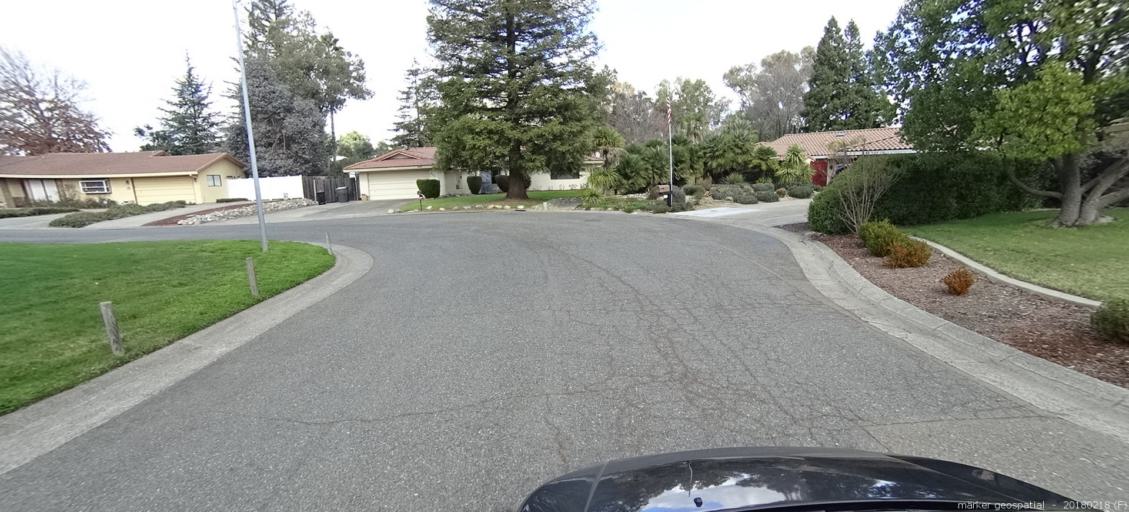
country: US
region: California
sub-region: Sacramento County
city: Orangevale
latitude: 38.6830
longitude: -121.2146
